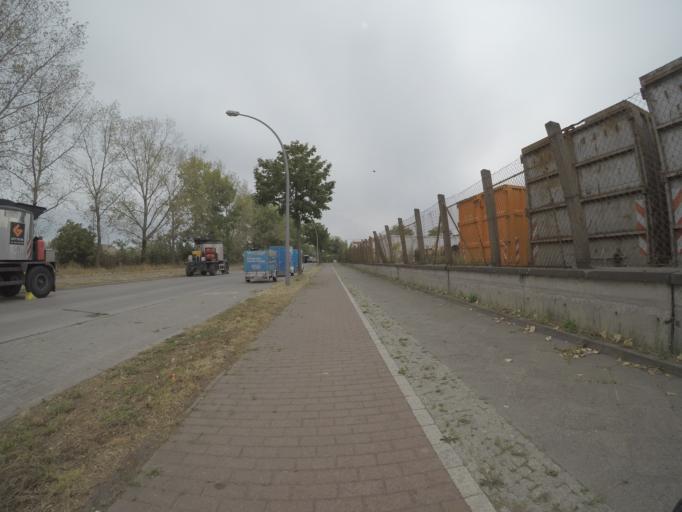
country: DE
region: Berlin
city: Alt-Hohenschoenhausen
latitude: 52.5455
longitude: 13.5256
